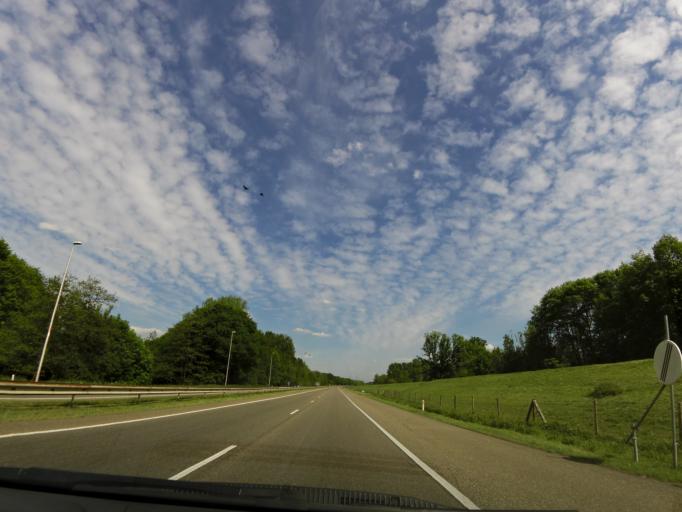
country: NL
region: Limburg
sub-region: Gemeente Leudal
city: Haelen
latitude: 51.2039
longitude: 5.9341
